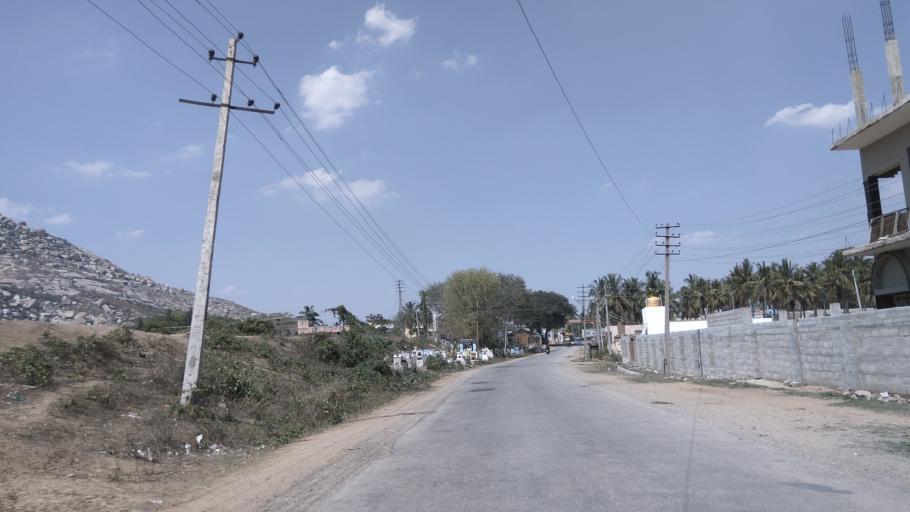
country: IN
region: Karnataka
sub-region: Kolar
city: Mulbagal
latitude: 13.1591
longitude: 78.3840
